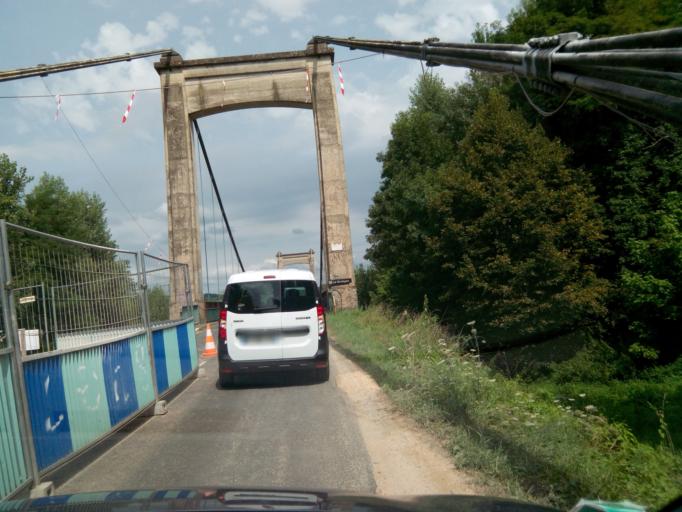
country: FR
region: Midi-Pyrenees
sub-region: Departement du Lot
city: Vayrac
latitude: 44.9148
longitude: 1.7425
